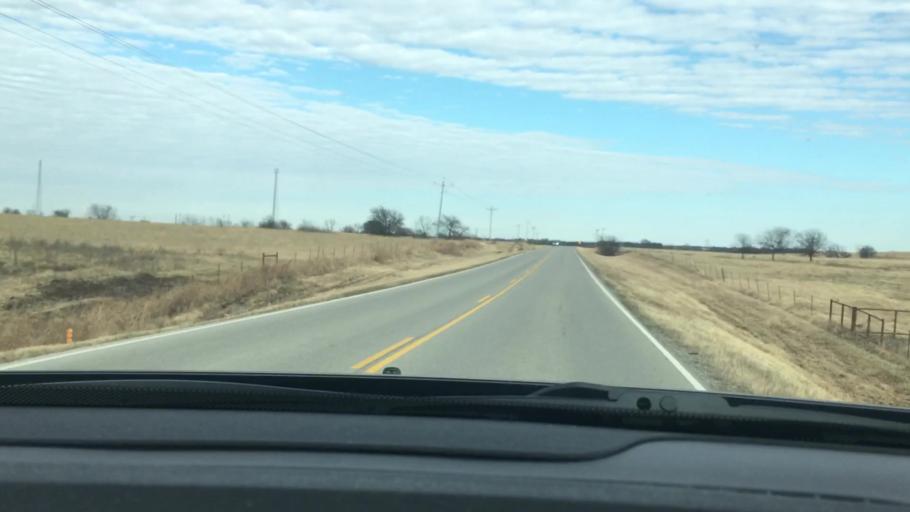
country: US
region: Oklahoma
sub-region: Garvin County
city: Pauls Valley
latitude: 34.7909
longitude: -97.1661
